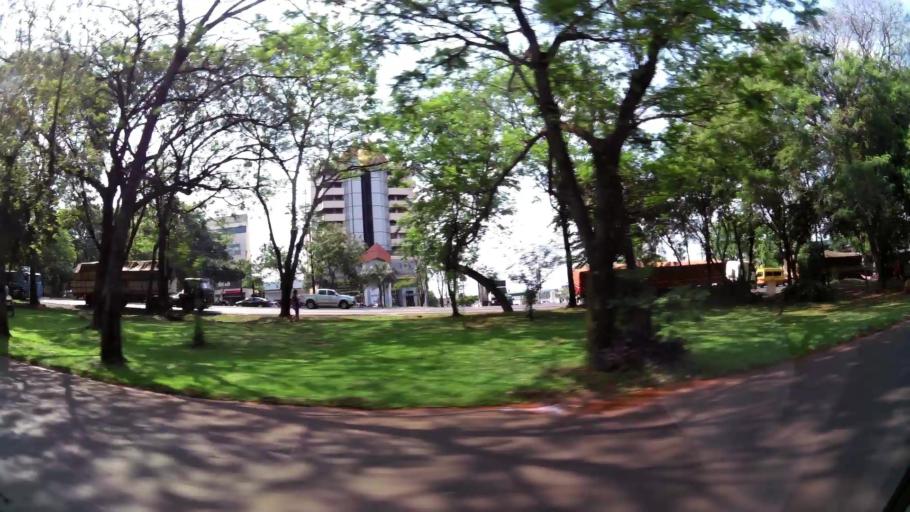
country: PY
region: Alto Parana
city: Ciudad del Este
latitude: -25.5105
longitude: -54.6210
